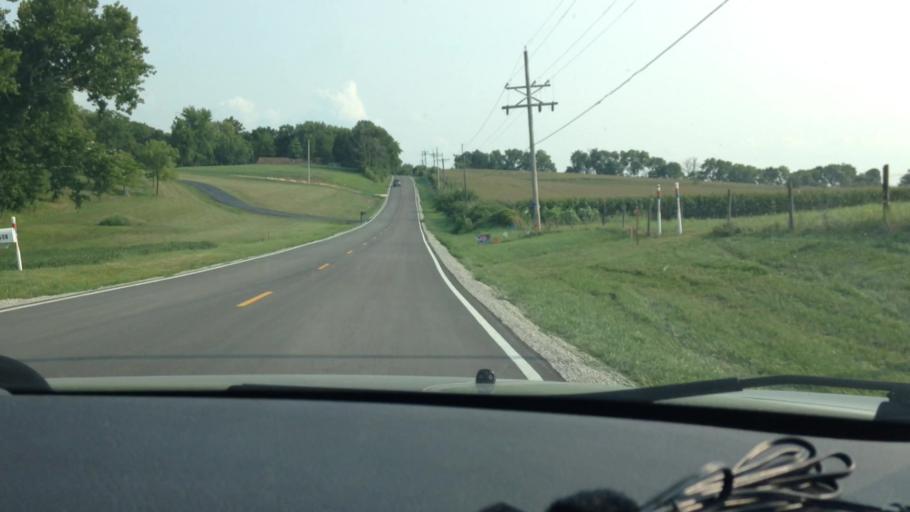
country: US
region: Missouri
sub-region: Platte County
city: Platte City
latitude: 39.3935
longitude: -94.7796
